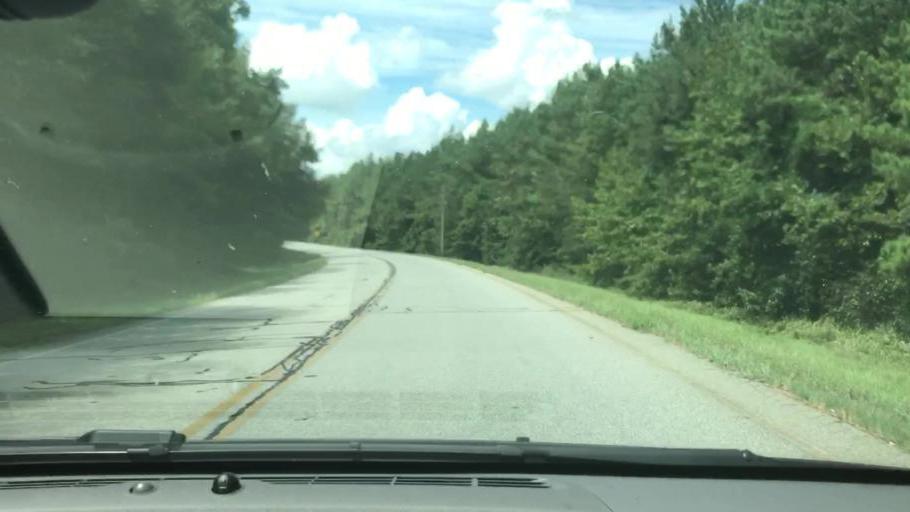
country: US
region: Georgia
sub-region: Stewart County
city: Lumpkin
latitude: 32.1494
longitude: -84.9028
